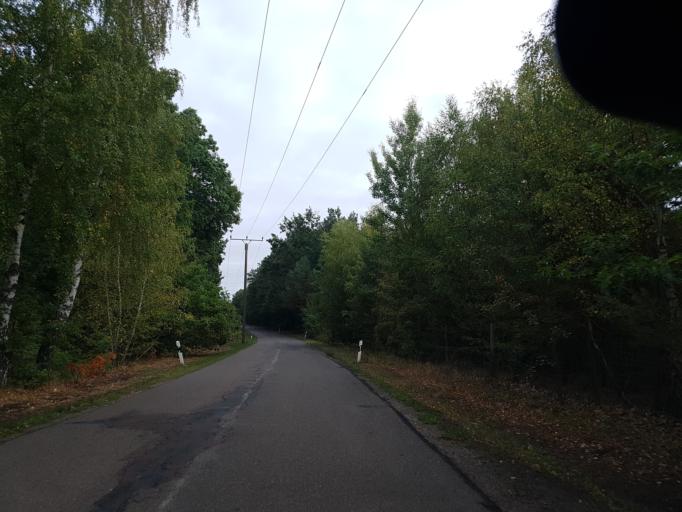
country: DE
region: Saxony-Anhalt
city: Rosslau
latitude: 51.9635
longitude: 12.3002
